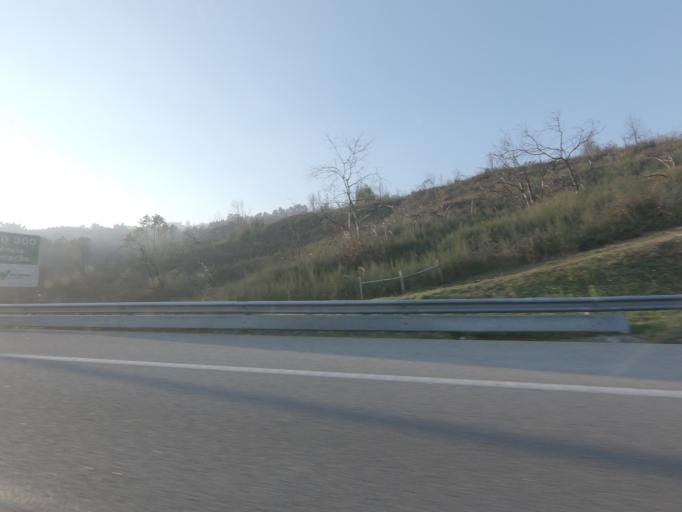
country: PT
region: Porto
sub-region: Amarante
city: Amarante
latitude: 41.2406
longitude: -8.1186
